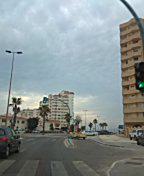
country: ES
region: Murcia
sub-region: Murcia
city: La Manga del Mar Menor
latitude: 37.7180
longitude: -0.7418
